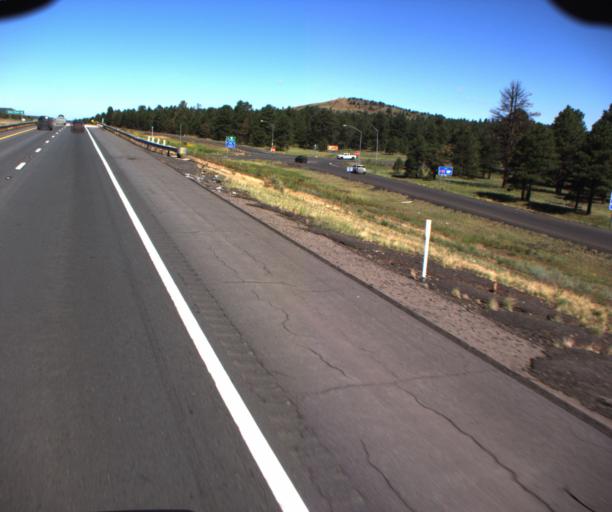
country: US
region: Arizona
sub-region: Coconino County
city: Williams
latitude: 35.2601
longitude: -112.1495
